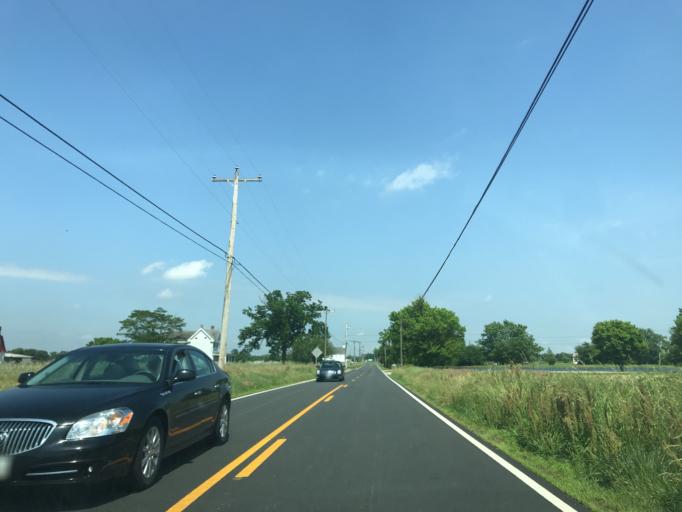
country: US
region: Maryland
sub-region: Dorchester County
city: Hurlock
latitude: 38.5728
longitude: -75.8048
